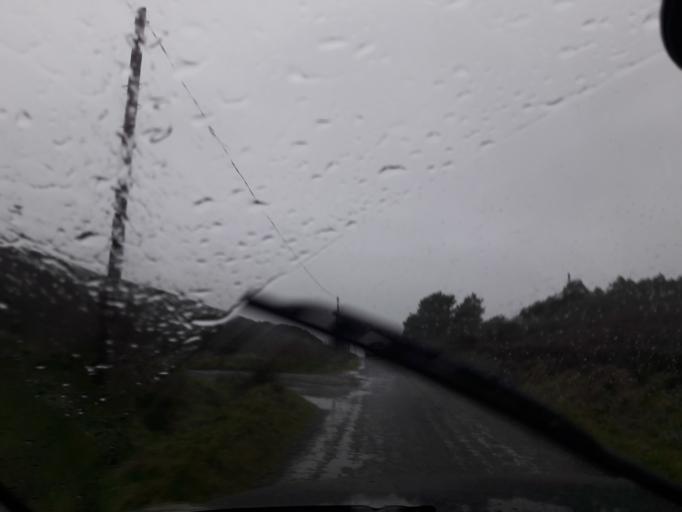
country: IE
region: Ulster
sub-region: County Donegal
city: Ramelton
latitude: 55.2625
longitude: -7.6395
